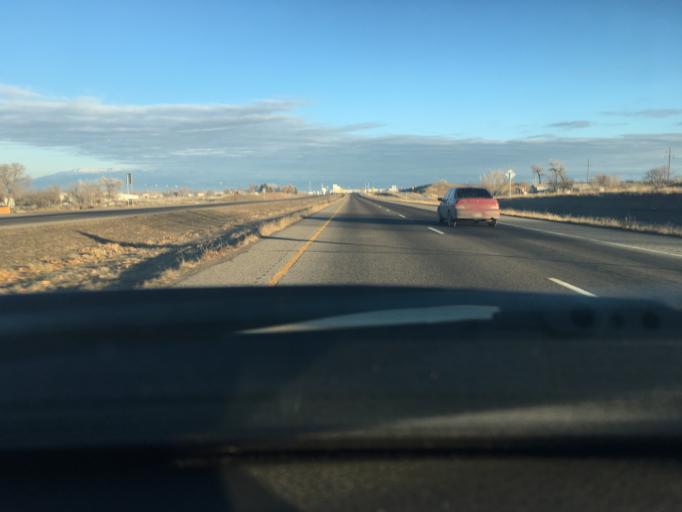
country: US
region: Colorado
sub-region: Montrose County
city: Olathe
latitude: 38.6001
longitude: -107.9731
